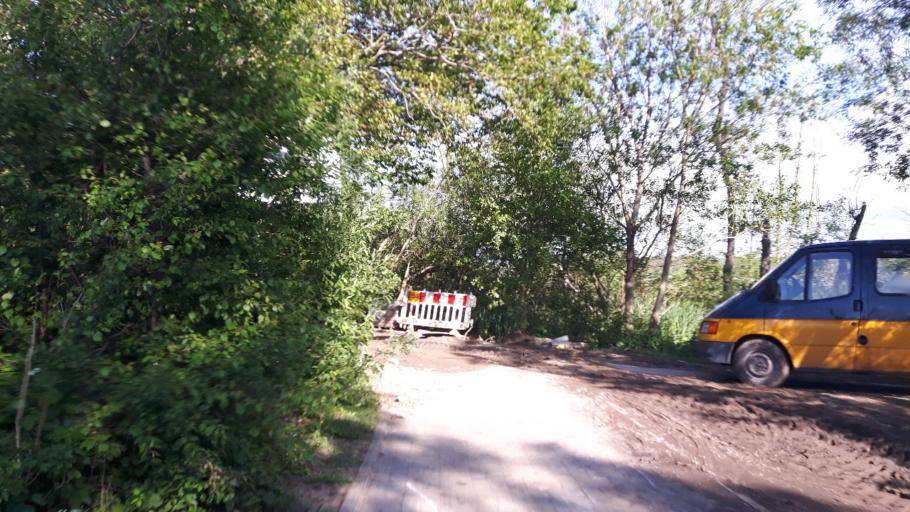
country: PL
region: West Pomeranian Voivodeship
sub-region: Powiat kolobrzeski
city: Kolobrzeg
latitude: 54.1967
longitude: 15.6429
